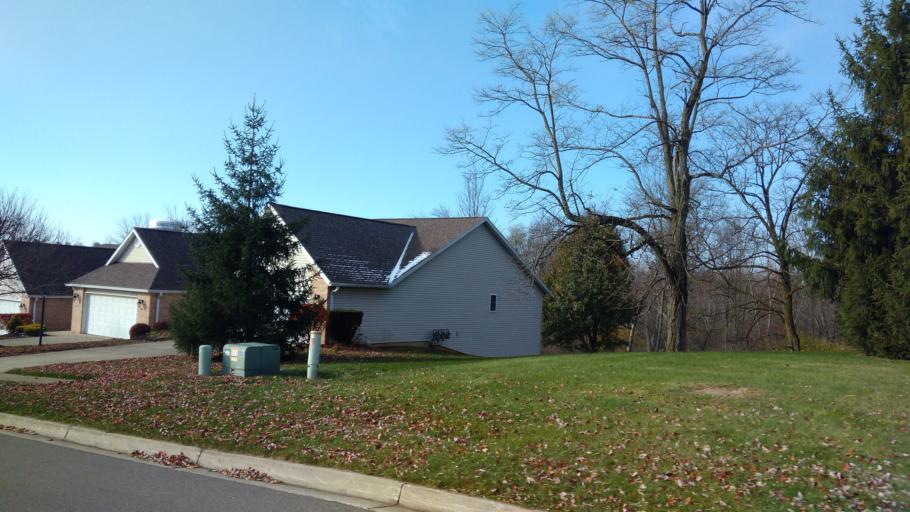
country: US
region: Ohio
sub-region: Richland County
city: Mansfield
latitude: 40.7156
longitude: -82.5429
